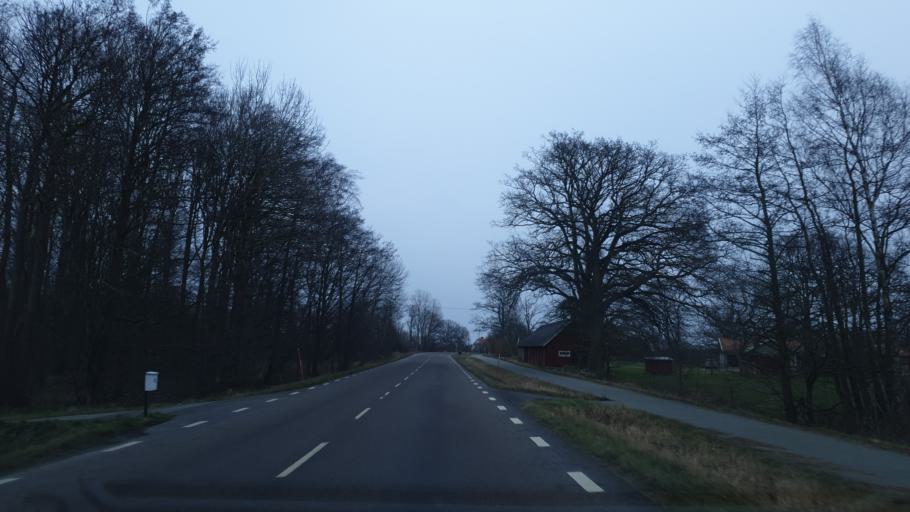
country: SE
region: Blekinge
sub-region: Karlskrona Kommun
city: Sturko
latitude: 56.1146
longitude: 15.6654
